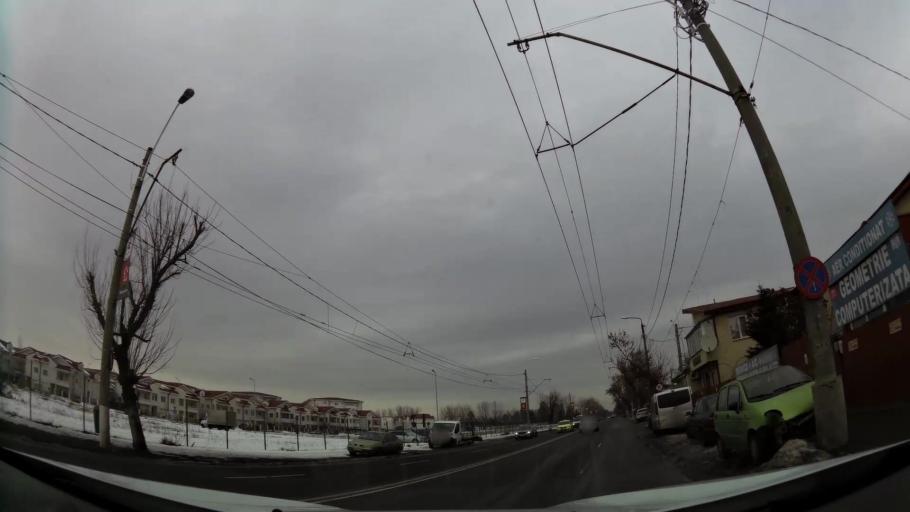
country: RO
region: Bucuresti
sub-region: Municipiul Bucuresti
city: Bucuresti
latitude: 44.4096
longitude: 26.0544
